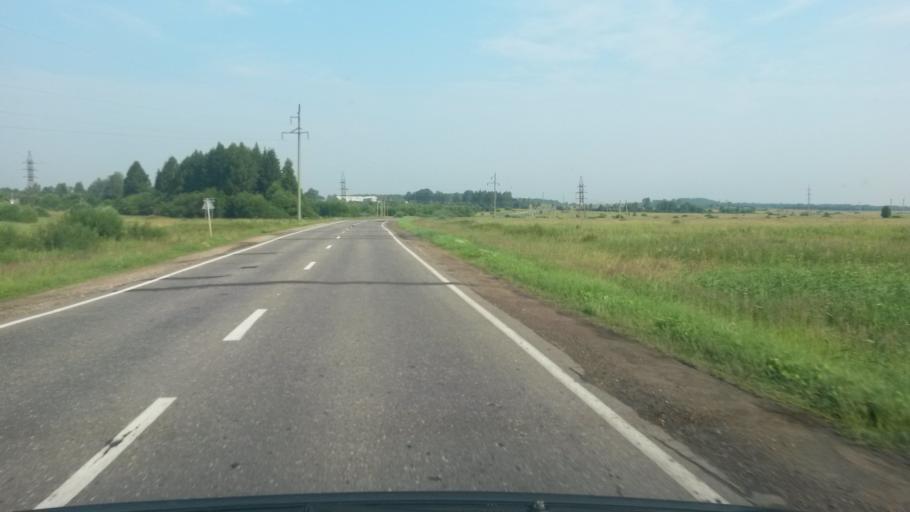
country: RU
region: Jaroslavl
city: Gavrilov-Yam
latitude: 57.3444
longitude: 39.7951
